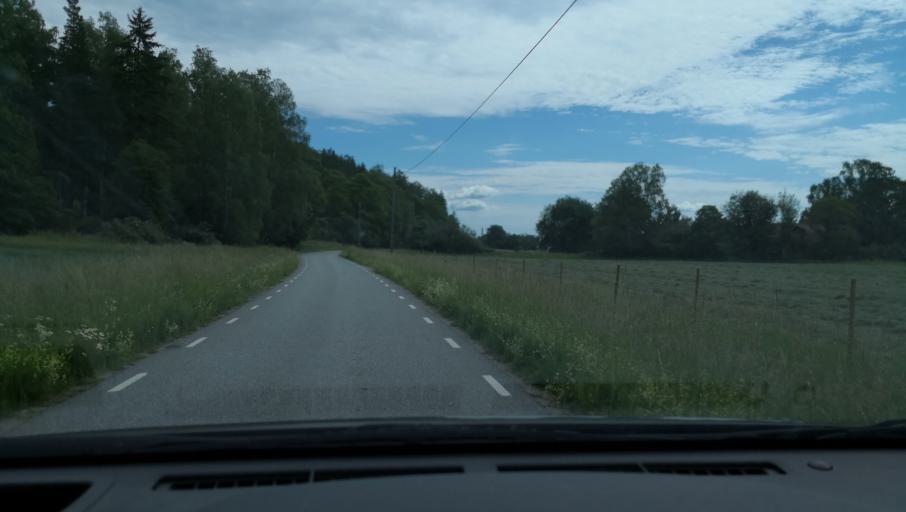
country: SE
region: Uppsala
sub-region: Enkopings Kommun
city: Orsundsbro
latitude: 59.6958
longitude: 17.4397
